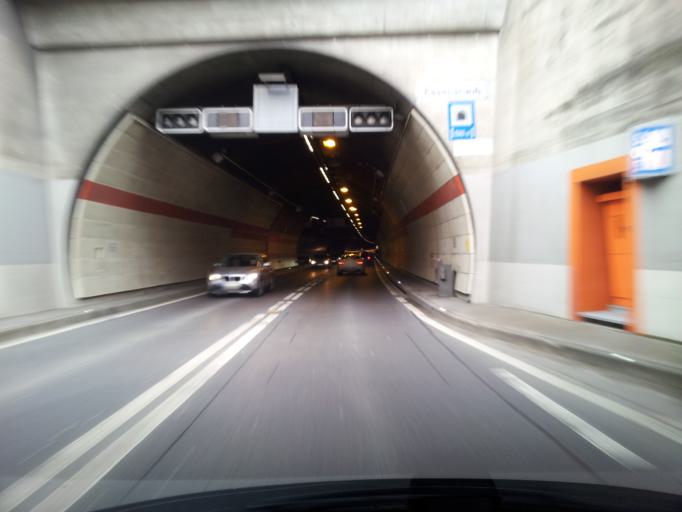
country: CH
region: Schaffhausen
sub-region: Bezirk Schaffhausen
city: Schaffhausen
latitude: 47.6938
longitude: 8.6254
